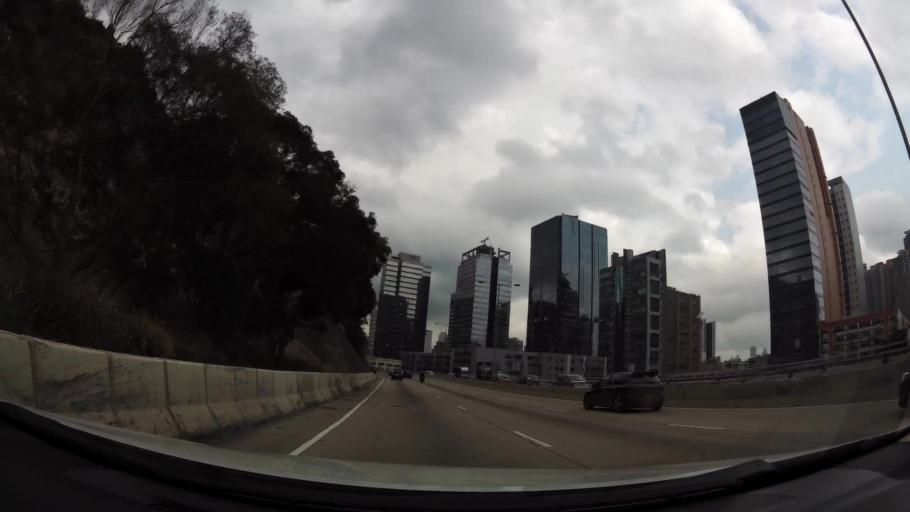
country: HK
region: Sham Shui Po
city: Sham Shui Po
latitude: 22.3400
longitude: 114.1458
